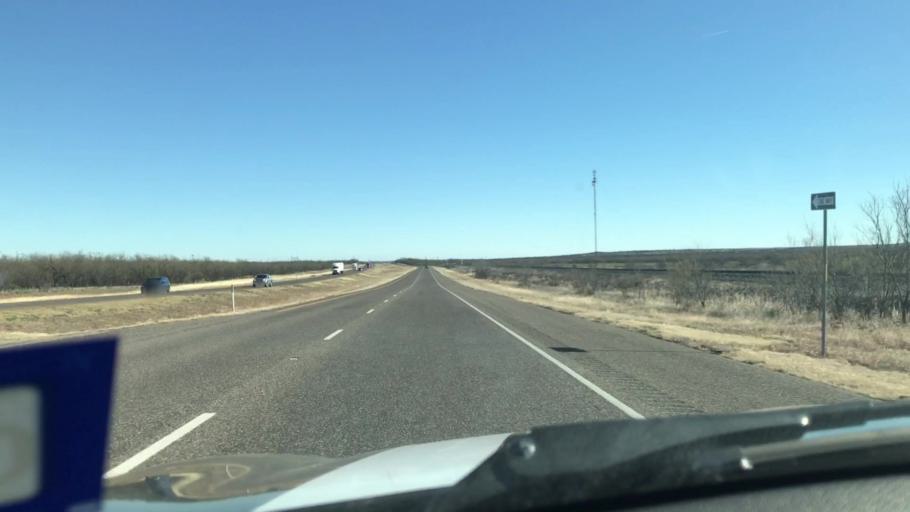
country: US
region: Texas
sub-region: Scurry County
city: Snyder
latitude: 32.8632
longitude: -101.0286
